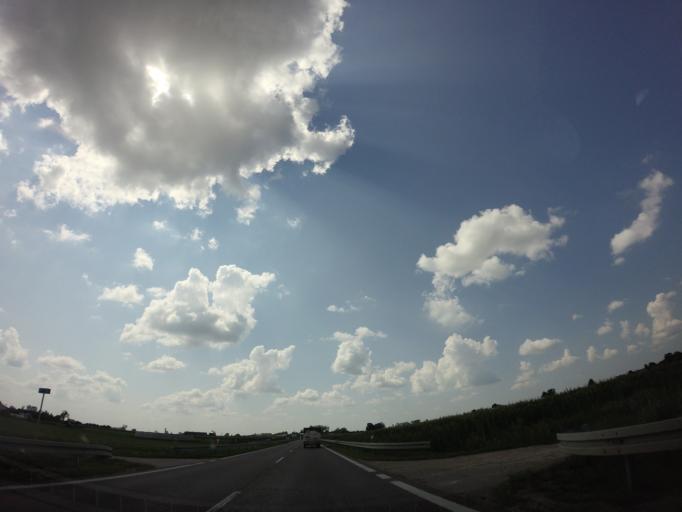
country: PL
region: Podlasie
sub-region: Powiat grajewski
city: Grajewo
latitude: 53.6749
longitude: 22.5815
